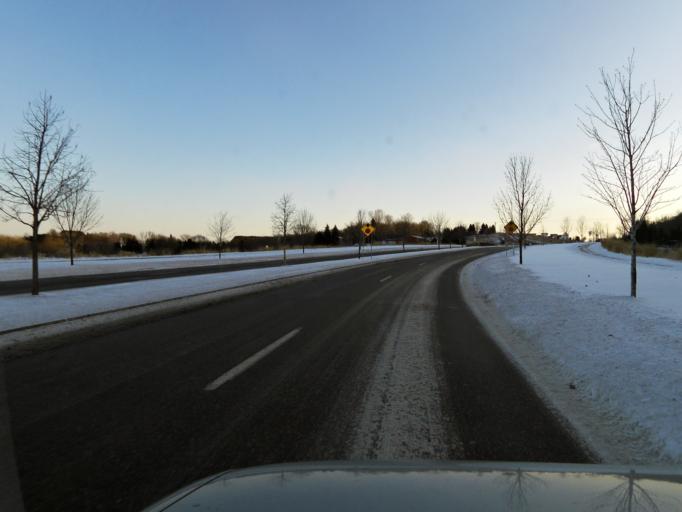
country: US
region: Minnesota
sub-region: Washington County
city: Lake Elmo
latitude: 44.9220
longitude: -92.8776
